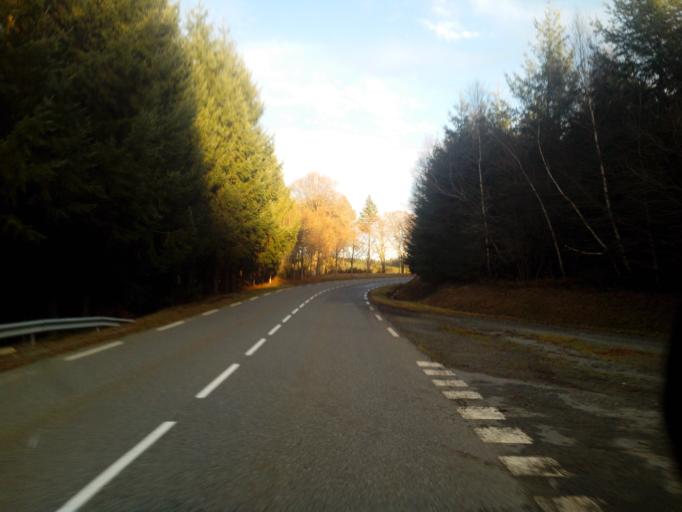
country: FR
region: Limousin
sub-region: Departement de la Correze
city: Meymac
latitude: 45.5732
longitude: 2.0717
